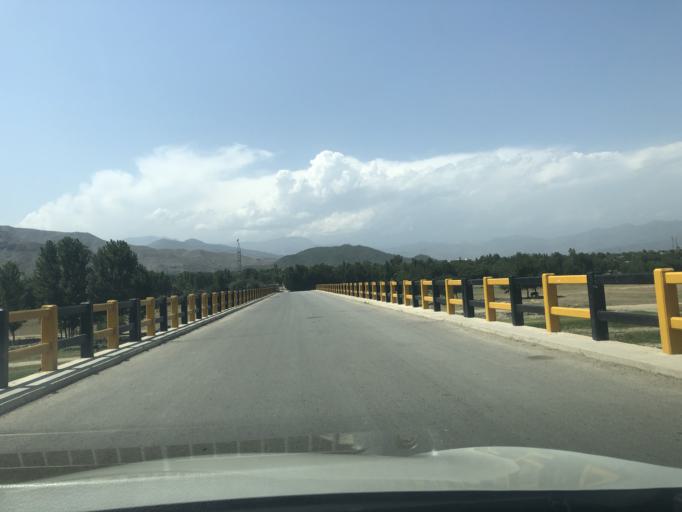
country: PK
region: Khyber Pakhtunkhwa
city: Timurgara
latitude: 34.7928
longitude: 71.6628
